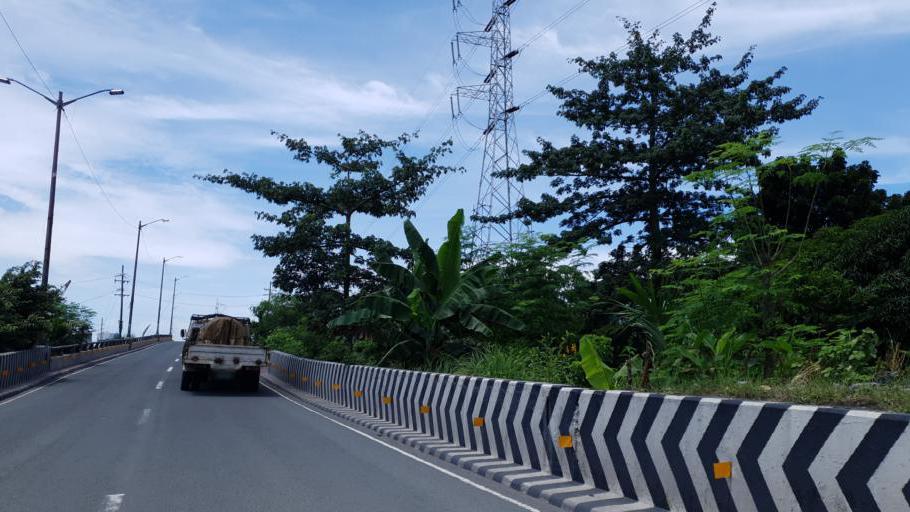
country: PH
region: Metro Manila
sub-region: San Juan
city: San Juan
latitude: 14.5922
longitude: 121.0106
